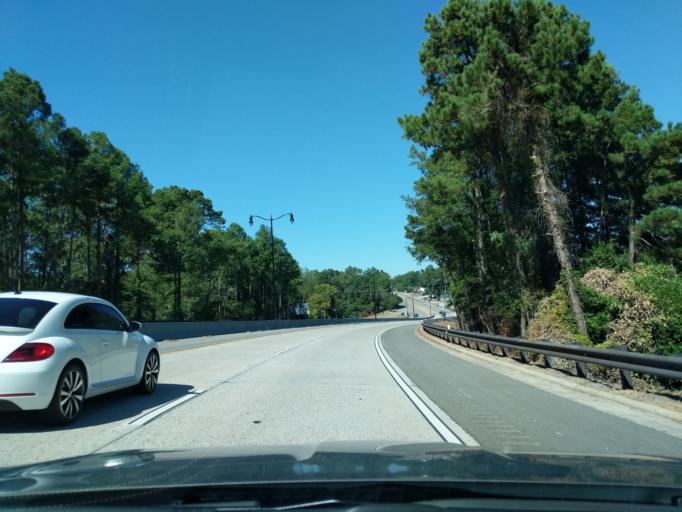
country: US
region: Georgia
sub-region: Richmond County
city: Augusta
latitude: 33.4896
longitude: -82.0098
